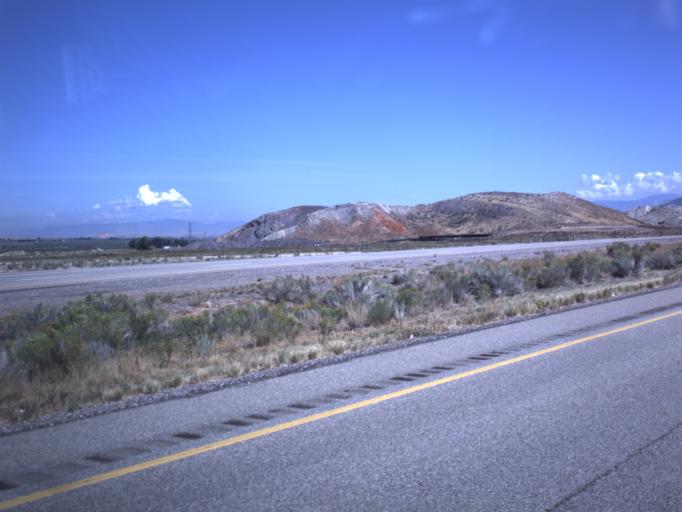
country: US
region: Utah
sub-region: Sevier County
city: Aurora
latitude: 38.8879
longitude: -111.9124
